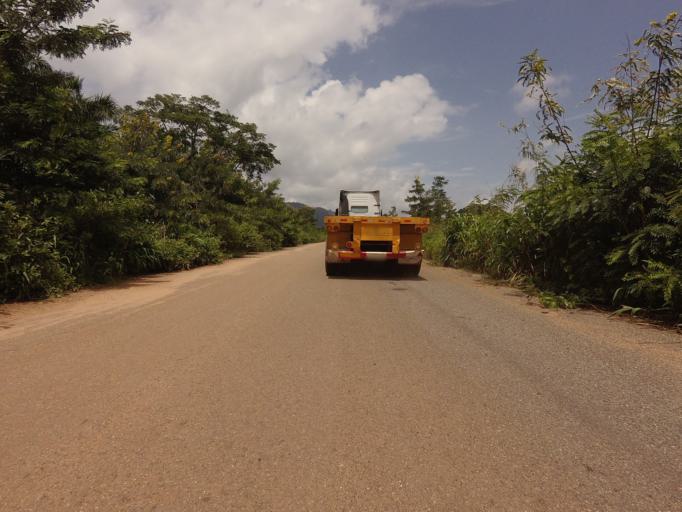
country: GH
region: Volta
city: Ho
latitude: 6.7807
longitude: 0.3656
